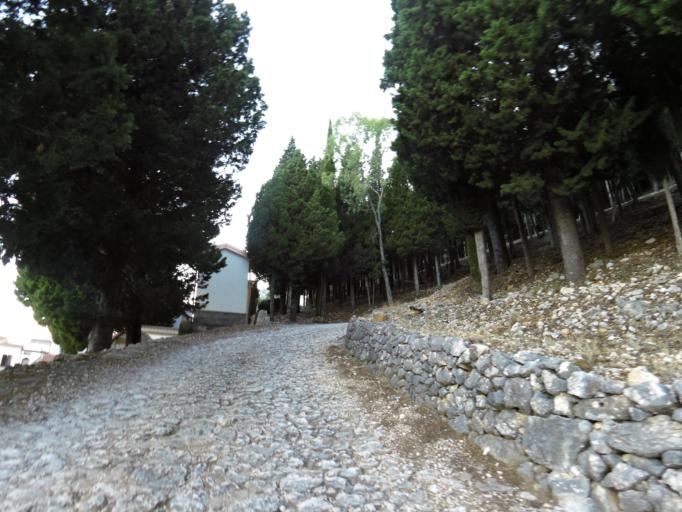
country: IT
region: Calabria
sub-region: Provincia di Reggio Calabria
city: Stilo
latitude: 38.4748
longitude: 16.4620
